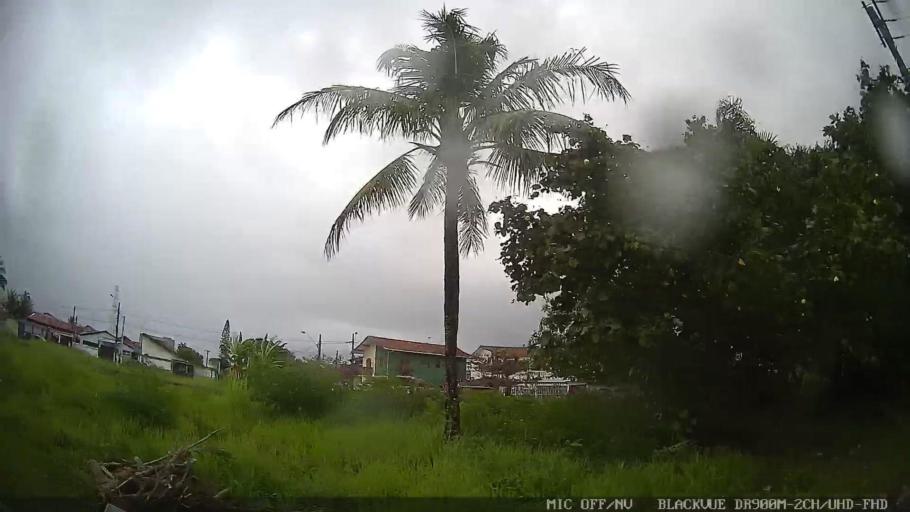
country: BR
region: Sao Paulo
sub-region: Mongagua
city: Mongagua
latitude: -24.1372
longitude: -46.7030
